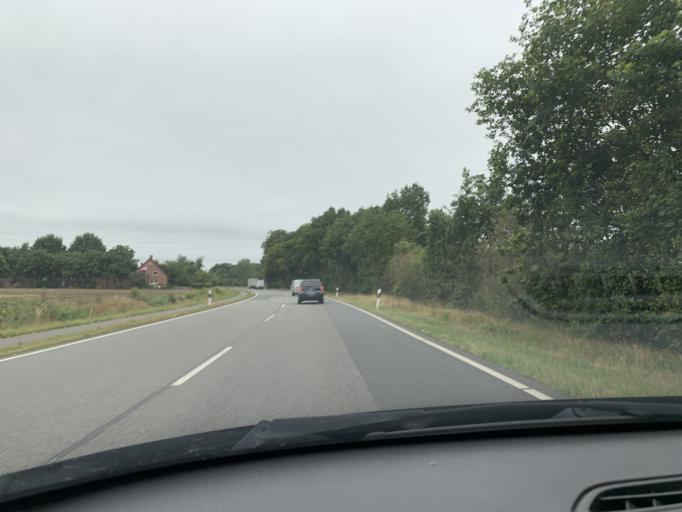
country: DE
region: Lower Saxony
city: Bawinkel
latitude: 52.5780
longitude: 7.3767
